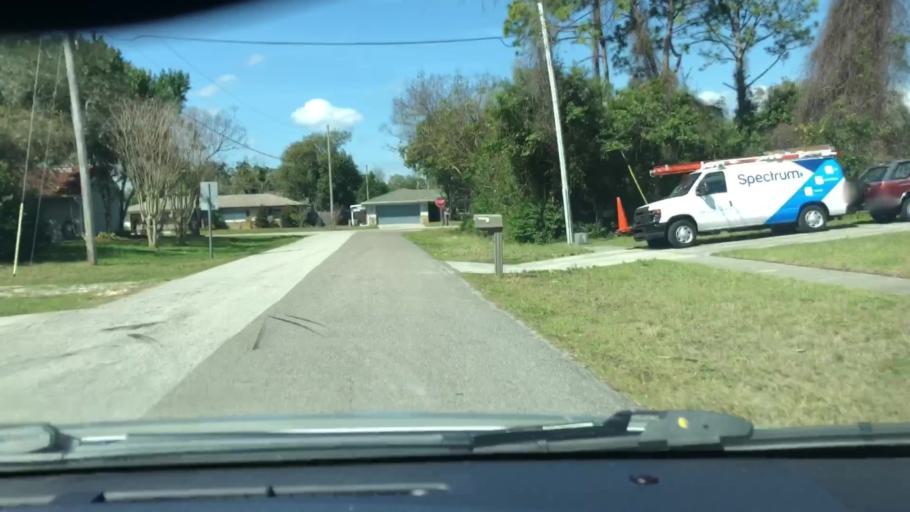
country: US
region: Florida
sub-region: Volusia County
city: Deltona
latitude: 28.8889
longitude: -81.2318
